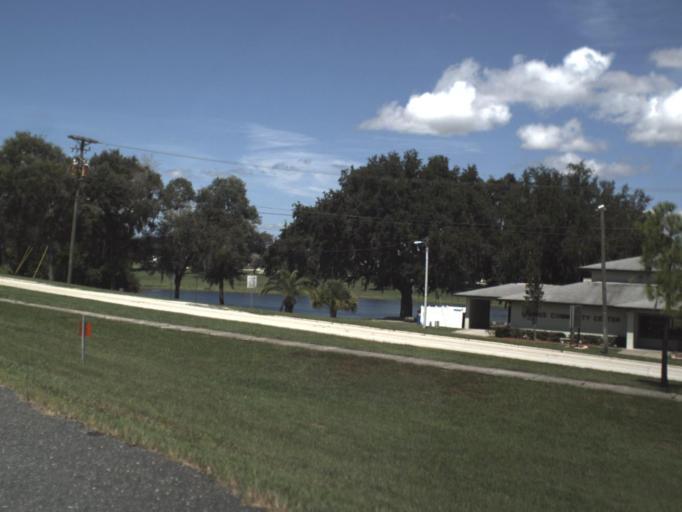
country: US
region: Florida
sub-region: Polk County
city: Dundee
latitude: 28.0219
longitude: -81.6126
